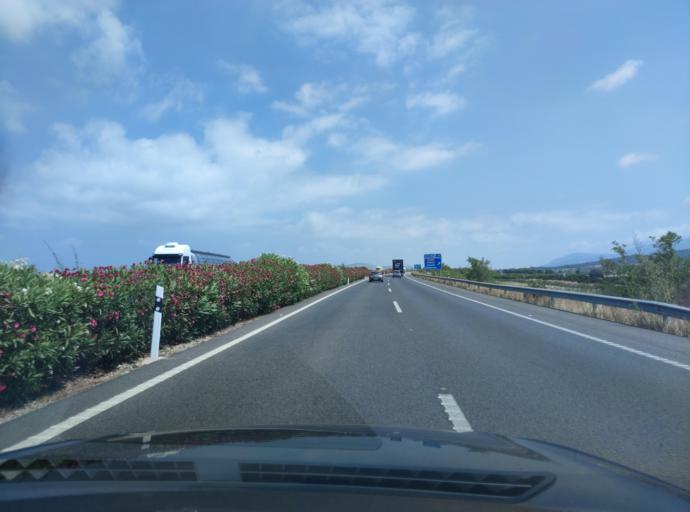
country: ES
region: Catalonia
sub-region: Provincia de Tarragona
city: Ulldecona
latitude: 40.5494
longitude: 0.4213
